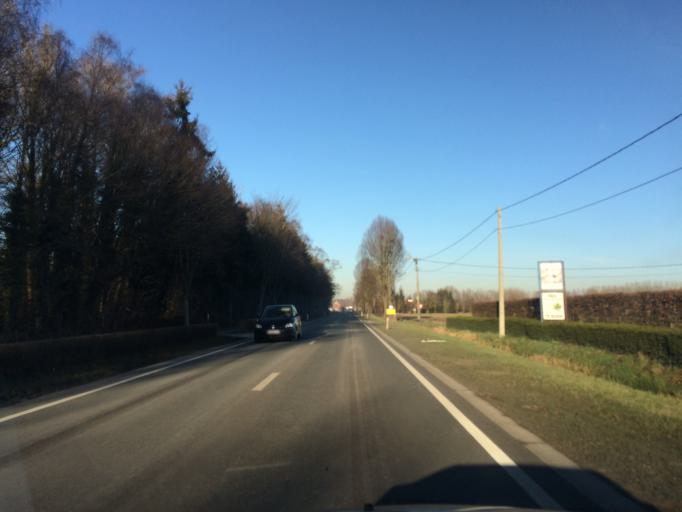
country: BE
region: Flanders
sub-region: Provincie West-Vlaanderen
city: Zedelgem
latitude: 51.1412
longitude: 3.1615
